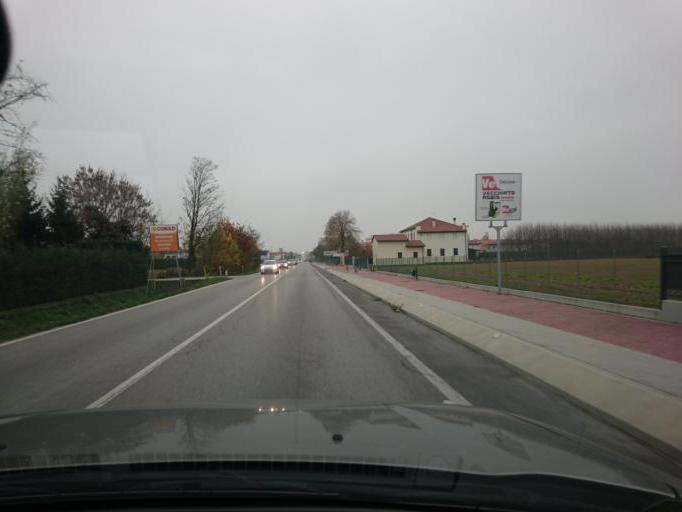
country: IT
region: Veneto
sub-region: Provincia di Padova
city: Legnaro
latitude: 45.3402
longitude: 11.9721
